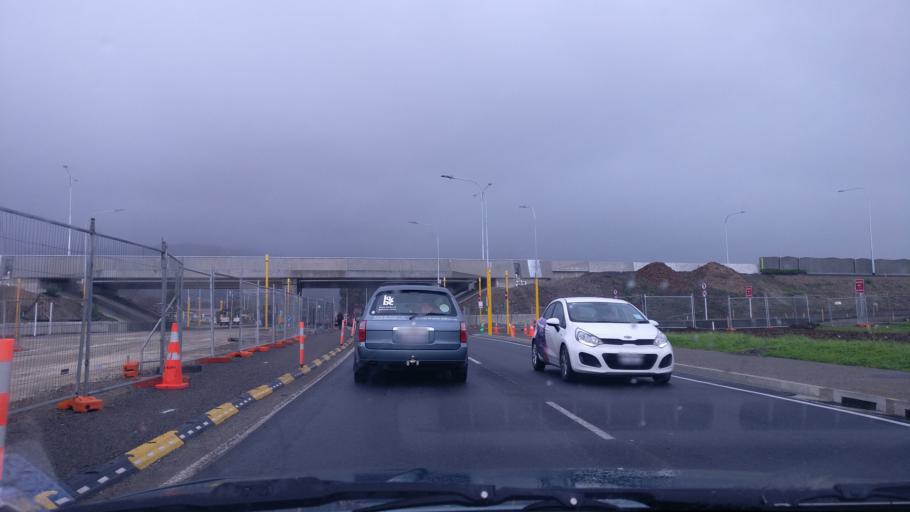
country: NZ
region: Wellington
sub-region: Kapiti Coast District
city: Paraparaumu
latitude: -40.9079
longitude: 174.9991
